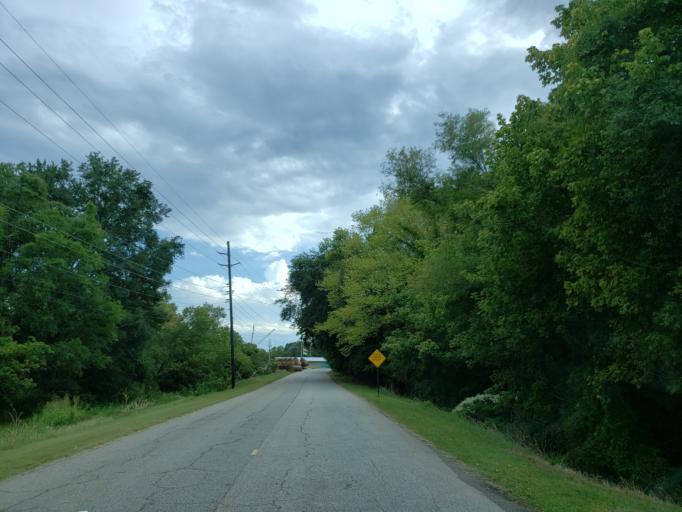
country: US
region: Georgia
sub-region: Bartow County
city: Cartersville
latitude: 34.1506
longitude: -84.8301
